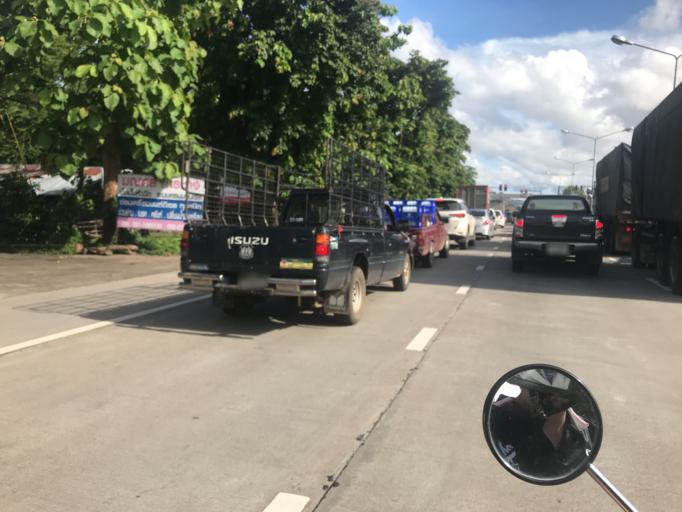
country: TH
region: Chiang Rai
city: Chiang Rai
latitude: 19.9385
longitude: 99.8453
